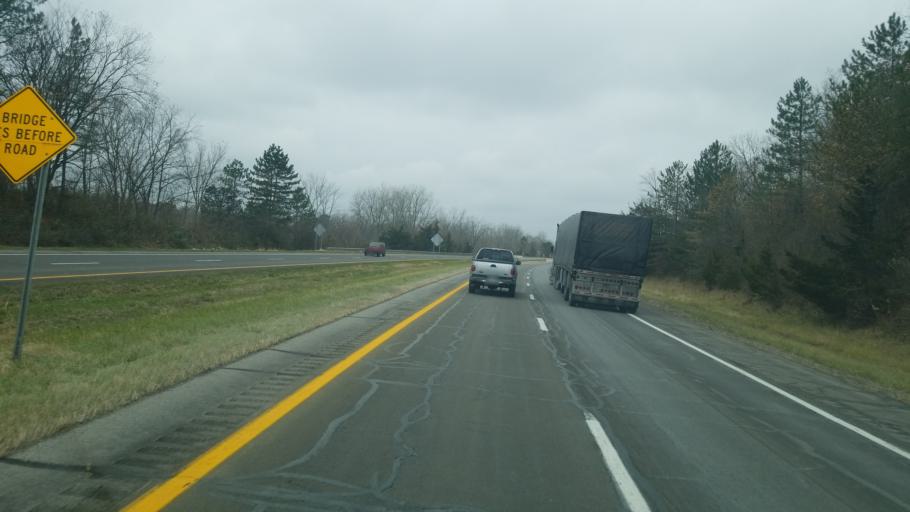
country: US
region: Ohio
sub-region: Huron County
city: Norwalk
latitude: 41.2262
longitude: -82.6430
